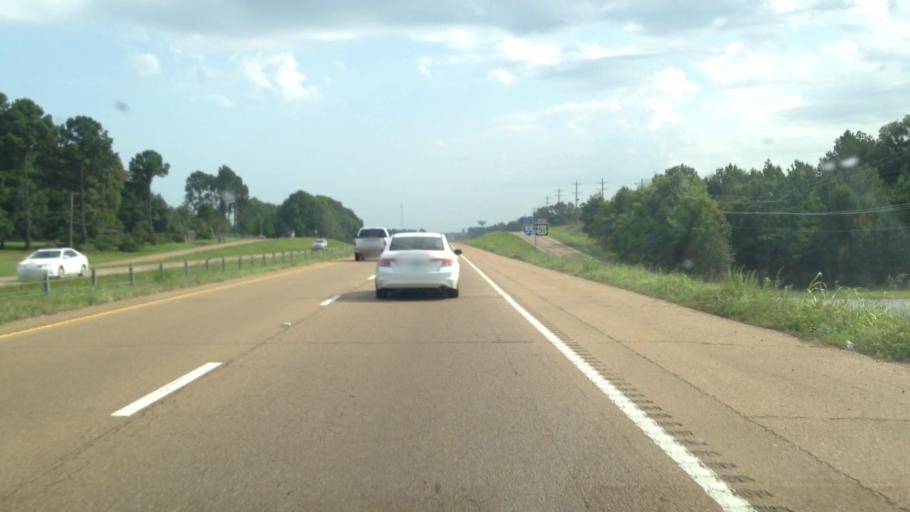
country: US
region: Mississippi
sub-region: Hinds County
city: Terry
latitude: 32.1373
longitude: -90.2842
